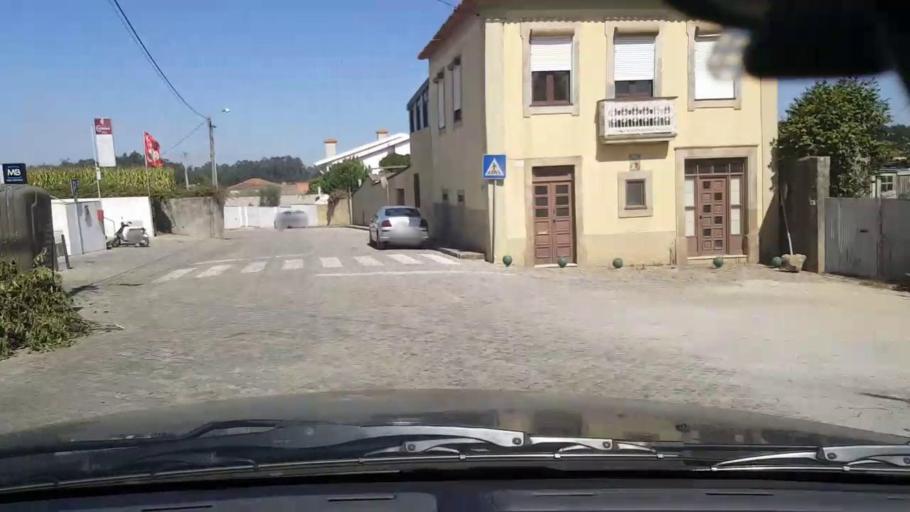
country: PT
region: Porto
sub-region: Matosinhos
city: Lavra
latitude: 41.2680
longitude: -8.6952
